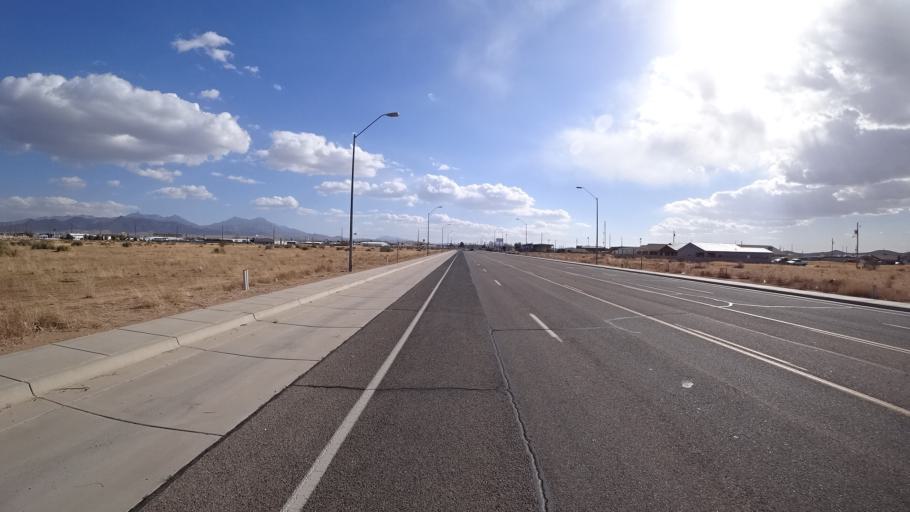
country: US
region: Arizona
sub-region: Mohave County
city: New Kingman-Butler
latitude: 35.2279
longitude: -114.0114
